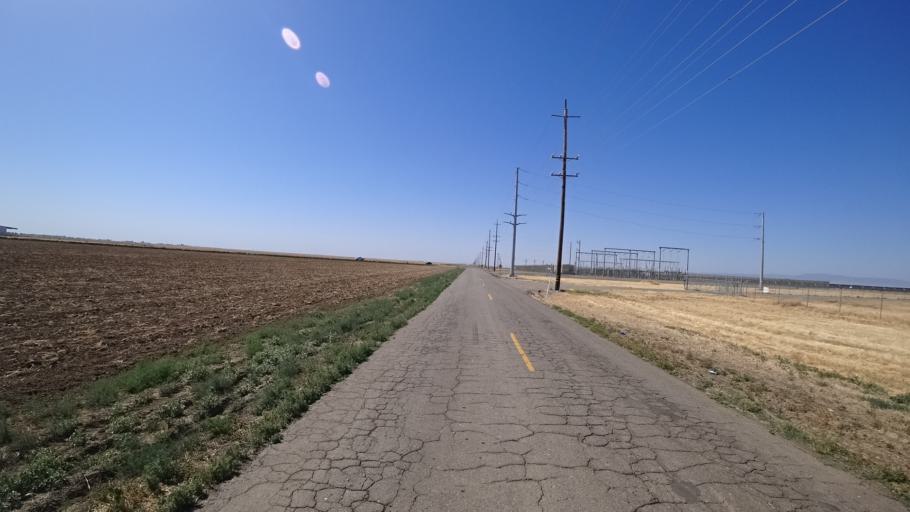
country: US
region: California
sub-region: Kings County
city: Lemoore Station
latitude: 36.2230
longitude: -119.9053
